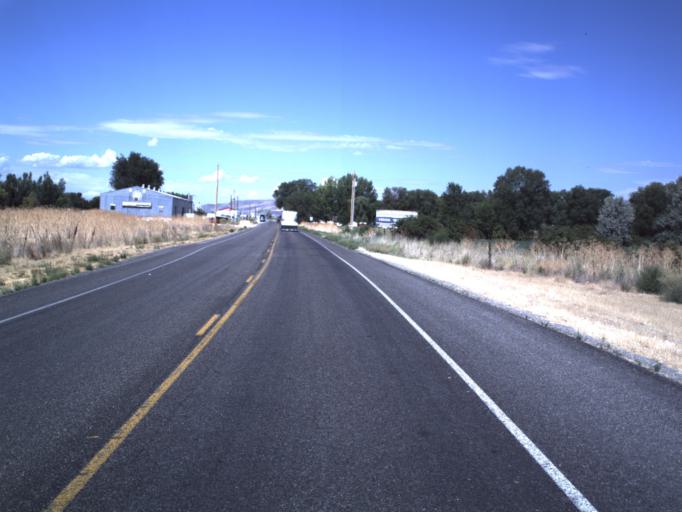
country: US
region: Utah
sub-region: Box Elder County
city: Honeyville
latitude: 41.5486
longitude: -112.1020
